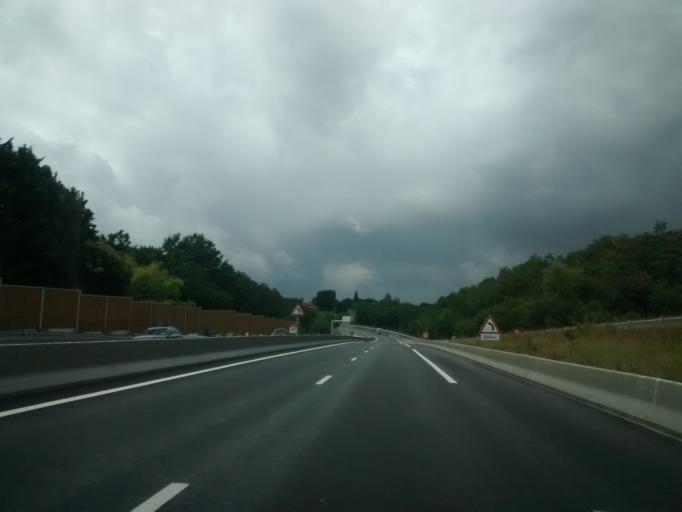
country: FR
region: Aquitaine
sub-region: Departement des Pyrenees-Atlantiques
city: Briscous
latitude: 43.4520
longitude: -1.3360
